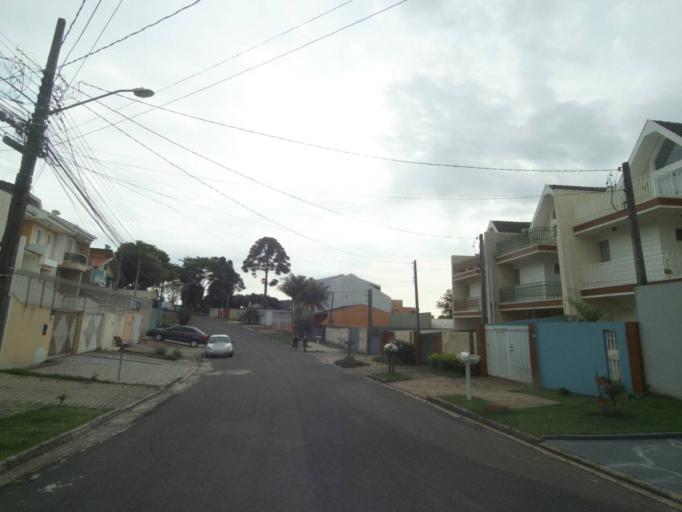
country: BR
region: Parana
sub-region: Curitiba
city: Curitiba
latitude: -25.3954
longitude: -49.2955
